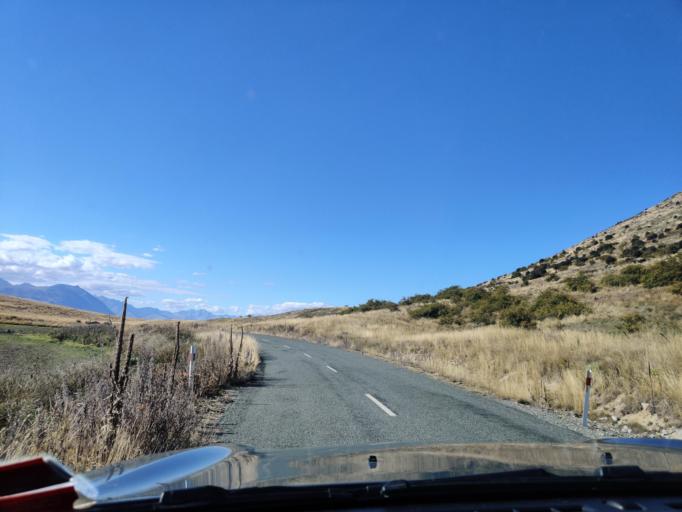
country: NZ
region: Canterbury
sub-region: Timaru District
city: Pleasant Point
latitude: -43.9781
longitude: 170.4633
